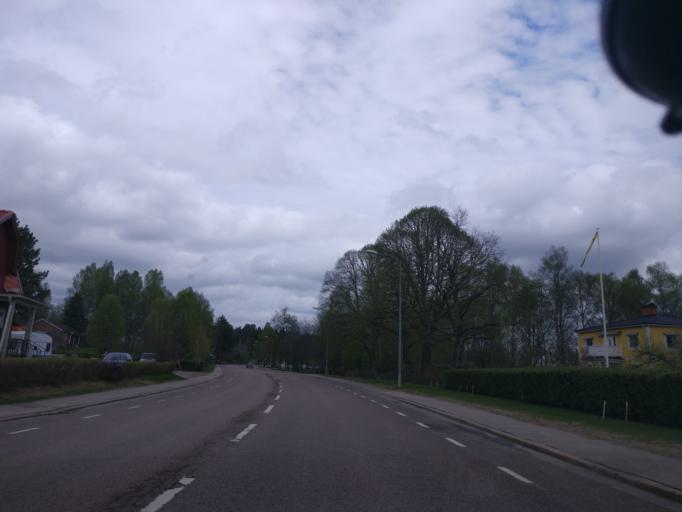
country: SE
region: Vaermland
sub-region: Hagfors Kommun
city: Ekshaerad
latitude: 60.1793
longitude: 13.4963
